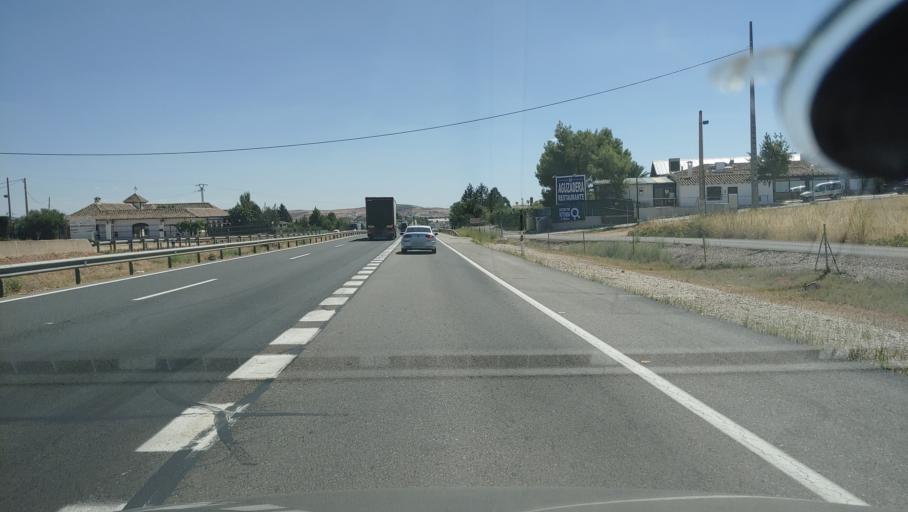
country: ES
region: Castille-La Mancha
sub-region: Provincia de Ciudad Real
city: Valdepenas
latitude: 38.7918
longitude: -3.3931
